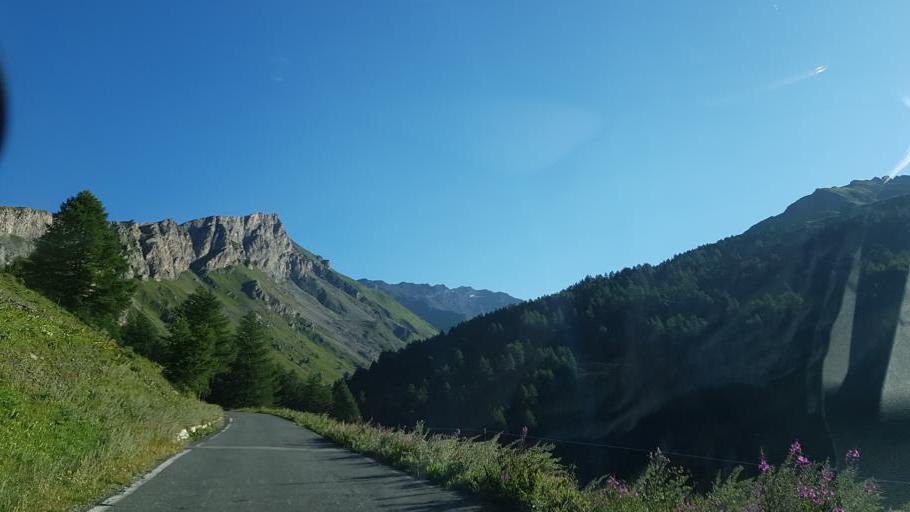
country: IT
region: Piedmont
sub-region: Provincia di Cuneo
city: Pontechianale
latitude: 44.6537
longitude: 6.9887
